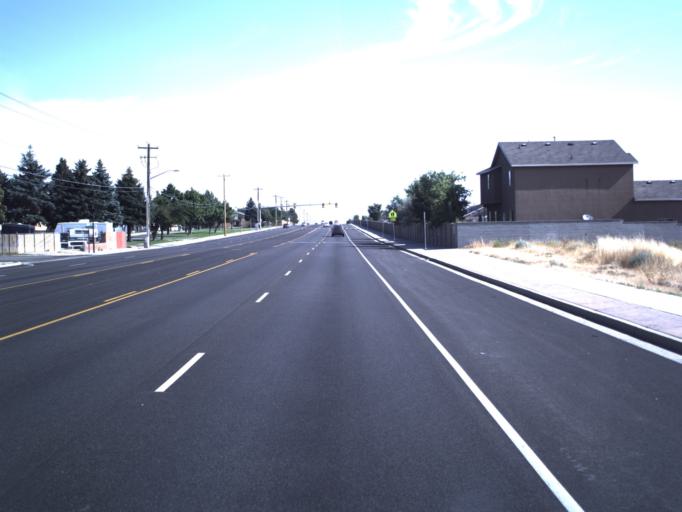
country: US
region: Utah
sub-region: Salt Lake County
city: Oquirrh
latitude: 40.6430
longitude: -112.0245
